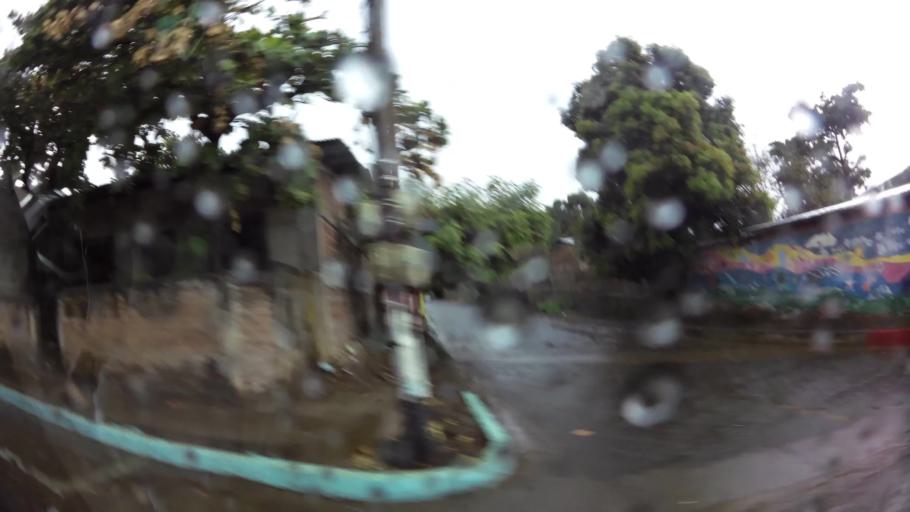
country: NI
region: Leon
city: Telica
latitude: 12.5240
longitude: -86.8586
